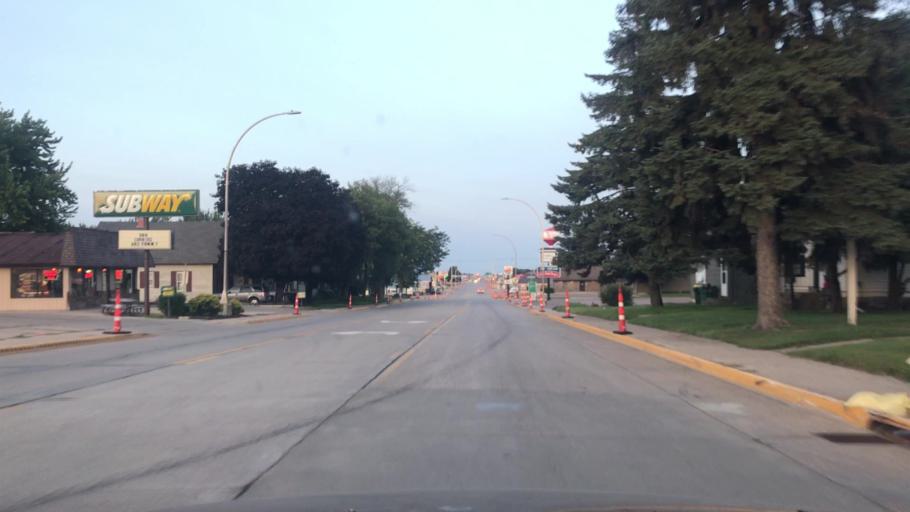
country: US
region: Minnesota
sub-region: Redwood County
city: Redwood Falls
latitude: 44.5414
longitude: -95.1146
